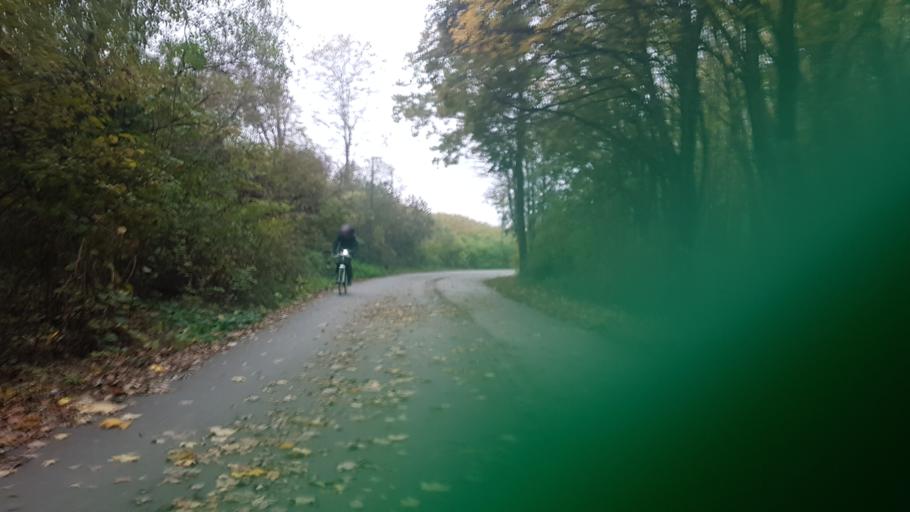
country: DE
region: Bavaria
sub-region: Upper Bavaria
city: Pasing
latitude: 48.1505
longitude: 11.4864
